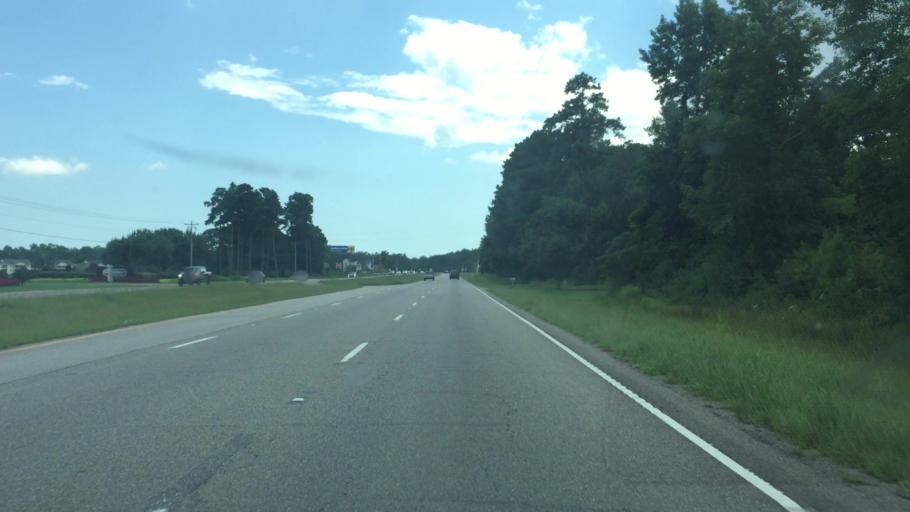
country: US
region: South Carolina
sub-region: Horry County
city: North Myrtle Beach
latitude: 33.9299
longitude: -78.7275
